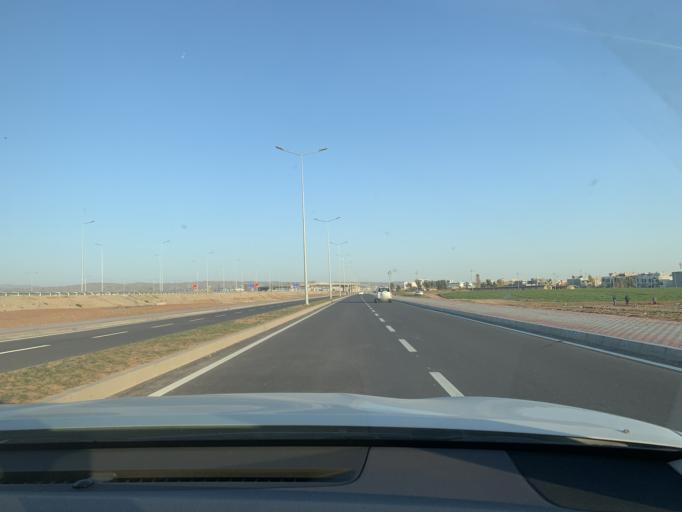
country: IQ
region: Arbil
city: Erbil
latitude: 36.2817
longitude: 44.0599
